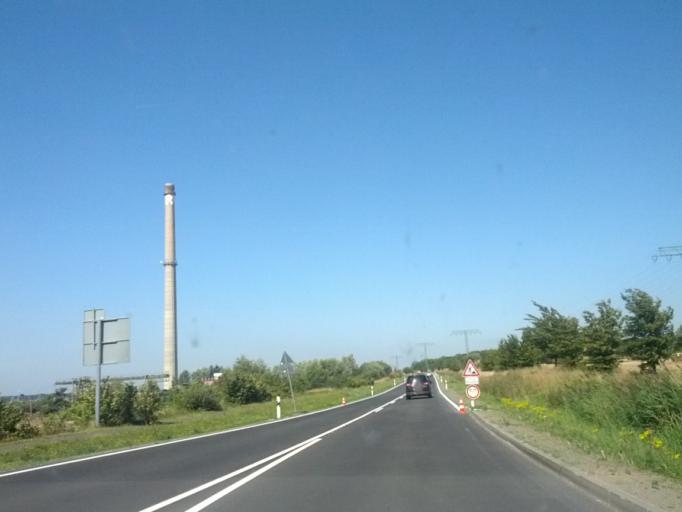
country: DE
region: Mecklenburg-Vorpommern
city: Sagard
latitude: 54.4930
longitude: 13.5774
